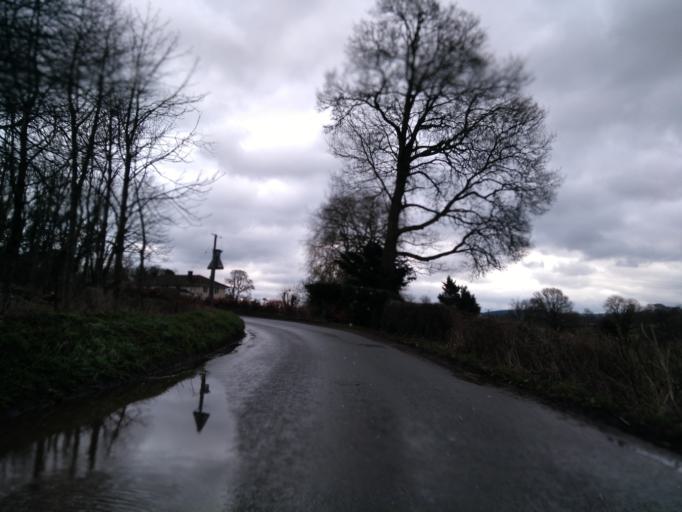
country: GB
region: England
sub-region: Devon
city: Crediton
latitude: 50.7954
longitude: -3.6335
